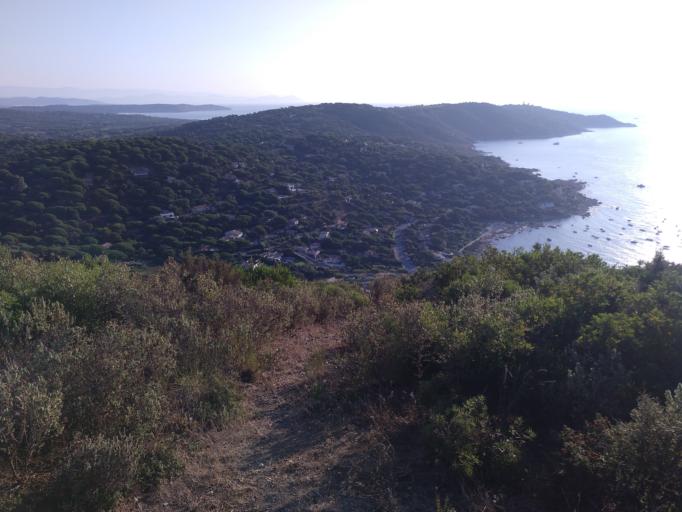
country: FR
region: Provence-Alpes-Cote d'Azur
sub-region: Departement du Var
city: Ramatuelle
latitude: 43.1847
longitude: 6.6375
